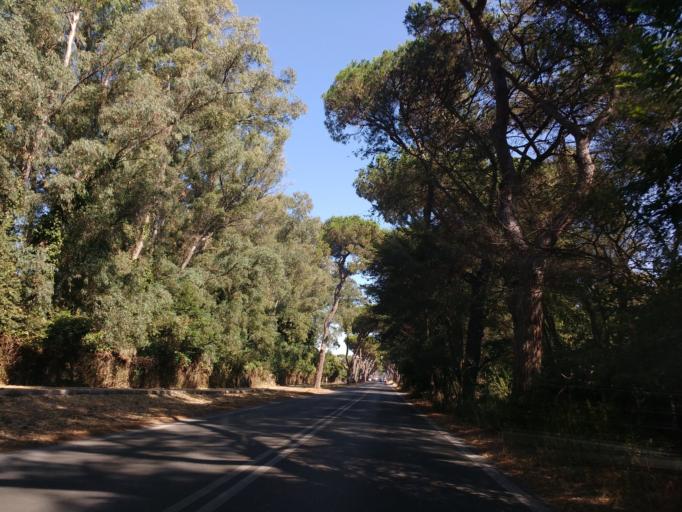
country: IT
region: Latium
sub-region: Citta metropolitana di Roma Capitale
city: Acilia-Castel Fusano-Ostia Antica
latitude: 41.7499
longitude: 12.3099
